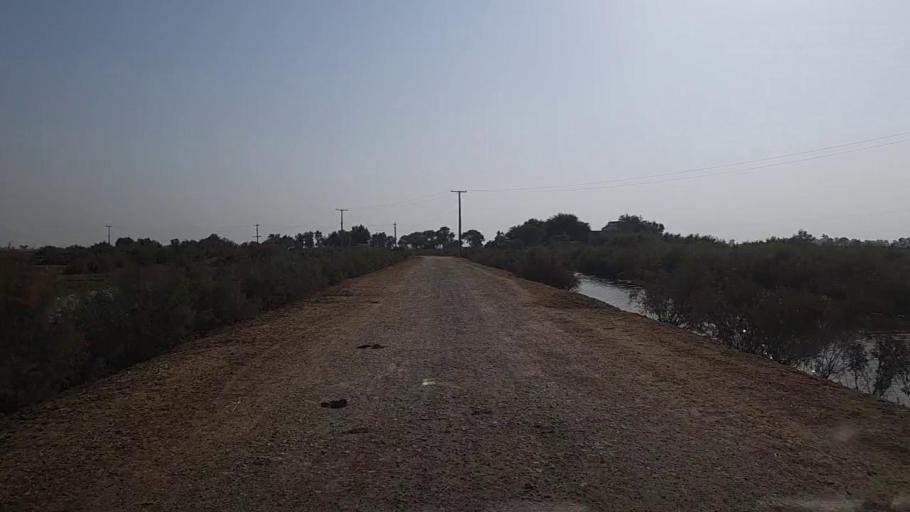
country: PK
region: Sindh
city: Kandhkot
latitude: 28.3822
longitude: 69.3358
